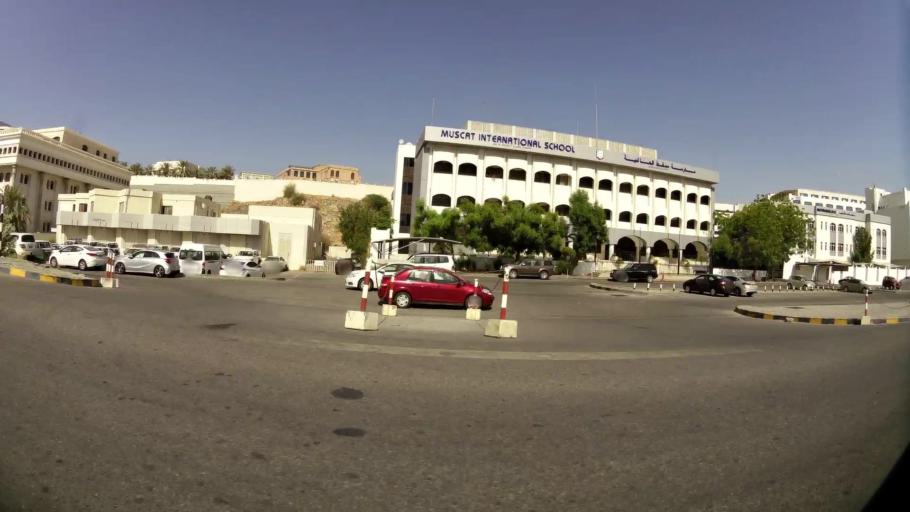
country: OM
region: Muhafazat Masqat
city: Muscat
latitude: 23.6066
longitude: 58.4913
